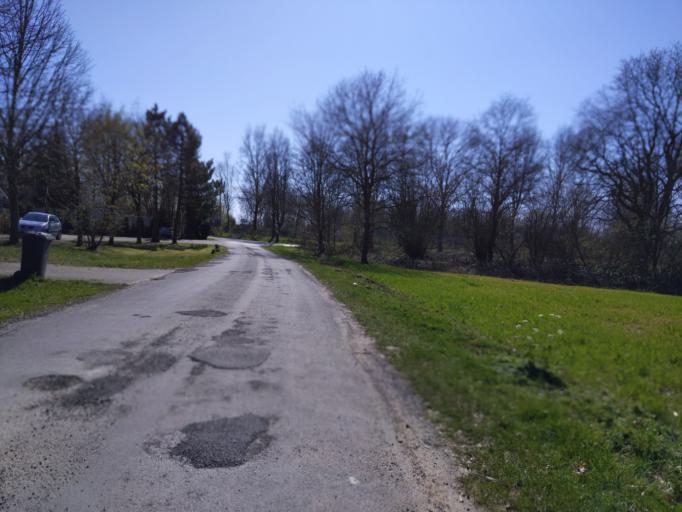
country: DE
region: North Rhine-Westphalia
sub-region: Regierungsbezirk Dusseldorf
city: Schermbeck
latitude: 51.6720
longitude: 6.8664
